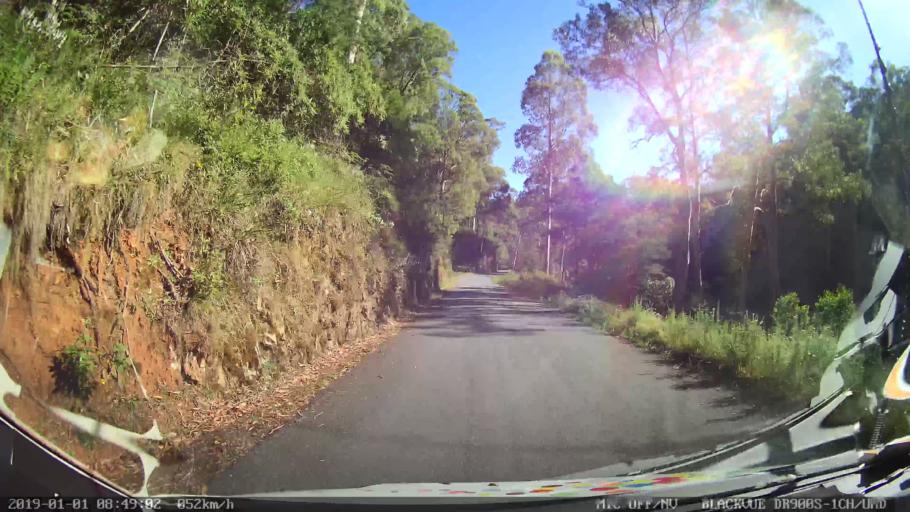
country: AU
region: New South Wales
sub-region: Snowy River
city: Jindabyne
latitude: -36.2851
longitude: 148.1987
